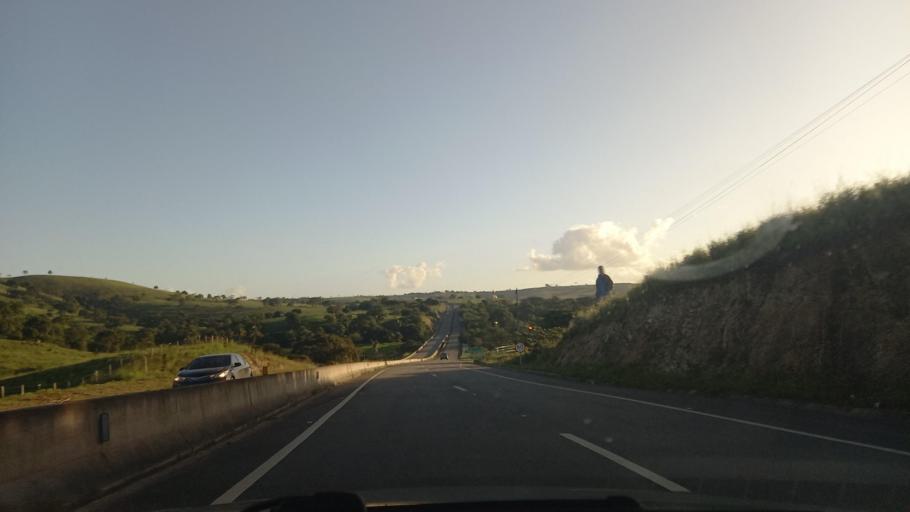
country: BR
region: Alagoas
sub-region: Limoeiro De Anadia
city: Limoeiro de Anadia
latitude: -9.7383
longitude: -36.4917
